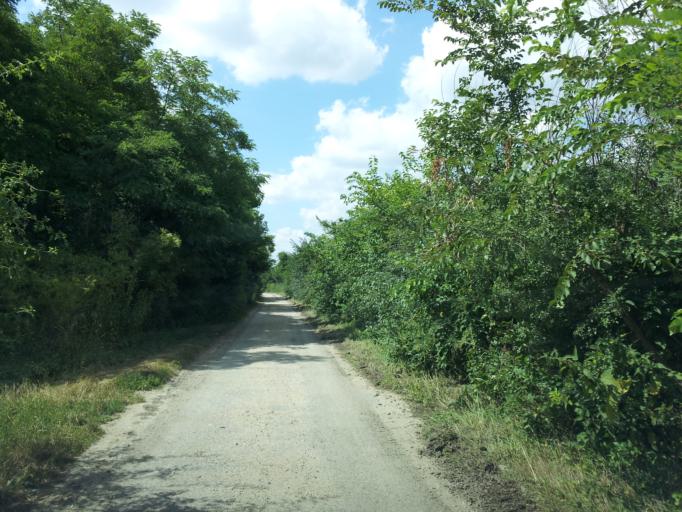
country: HU
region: Veszprem
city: Balatonkenese
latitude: 47.0524
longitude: 18.0701
